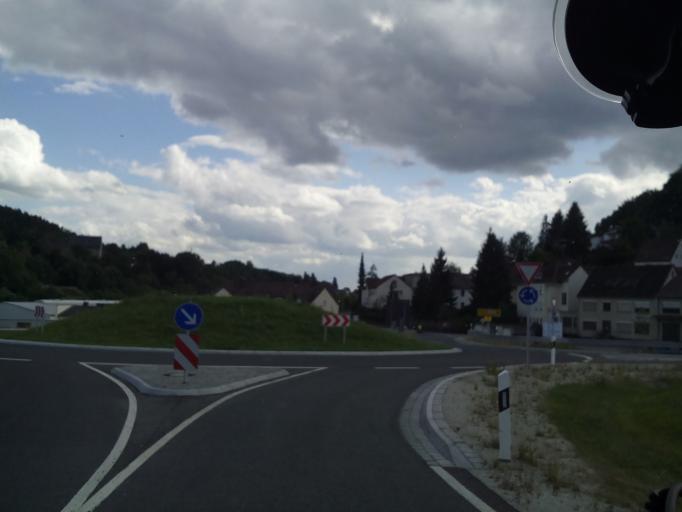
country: DE
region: Bavaria
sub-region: Upper Franconia
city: Rodental
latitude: 50.3056
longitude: 11.0607
